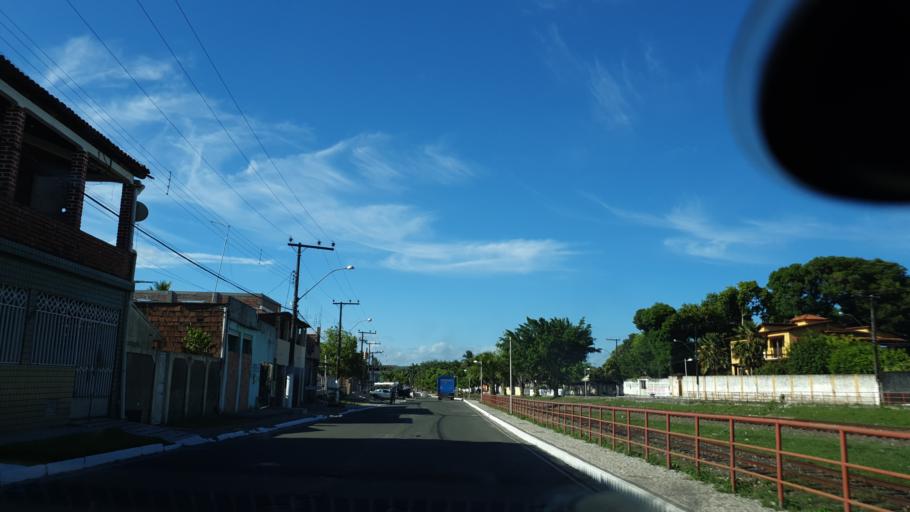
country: BR
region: Bahia
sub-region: Mata De Sao Joao
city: Mata de Sao Joao
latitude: -12.6124
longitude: -38.2975
